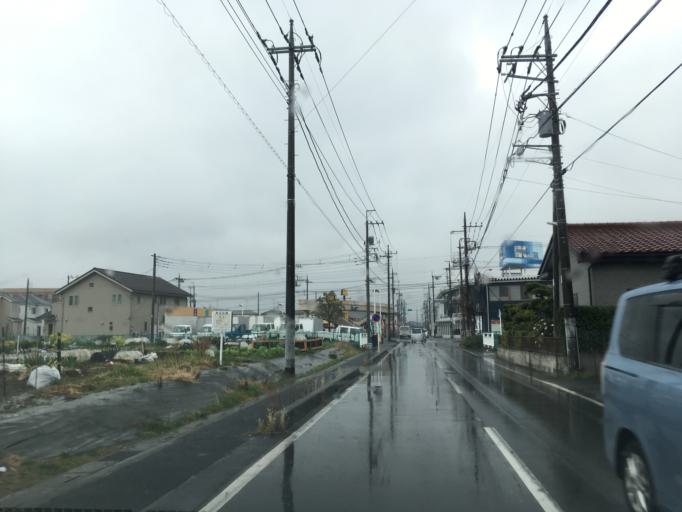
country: JP
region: Saitama
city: Koshigaya
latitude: 35.8905
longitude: 139.7719
